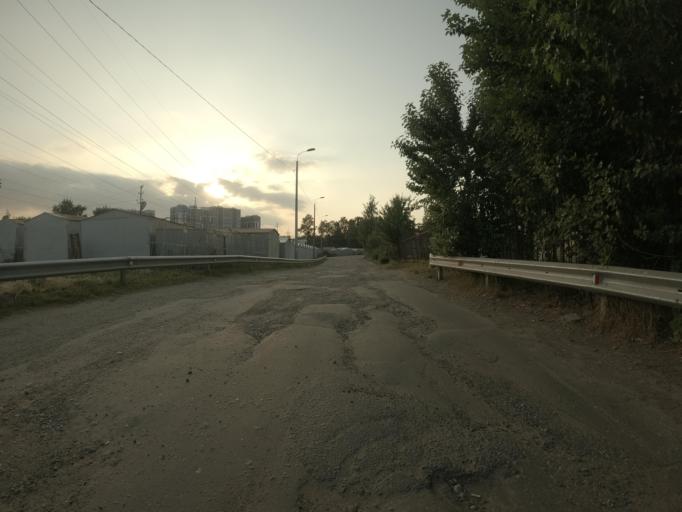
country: RU
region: St.-Petersburg
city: Krasnogvargeisky
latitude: 59.9549
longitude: 30.4576
